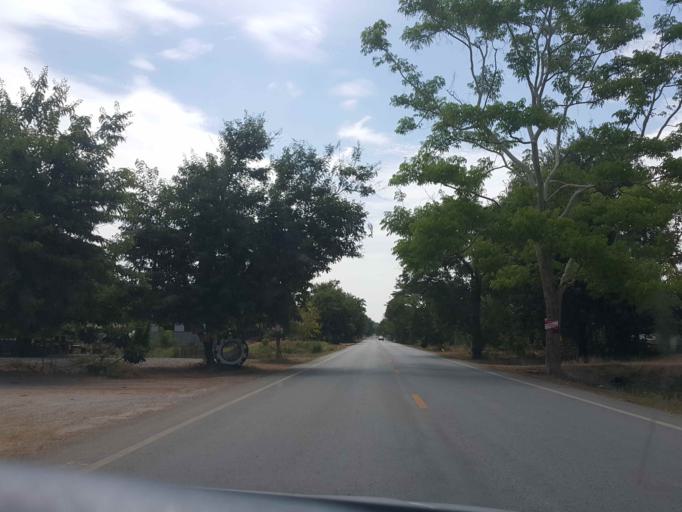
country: TH
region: Sukhothai
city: Thung Saliam
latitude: 17.3348
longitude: 99.5603
